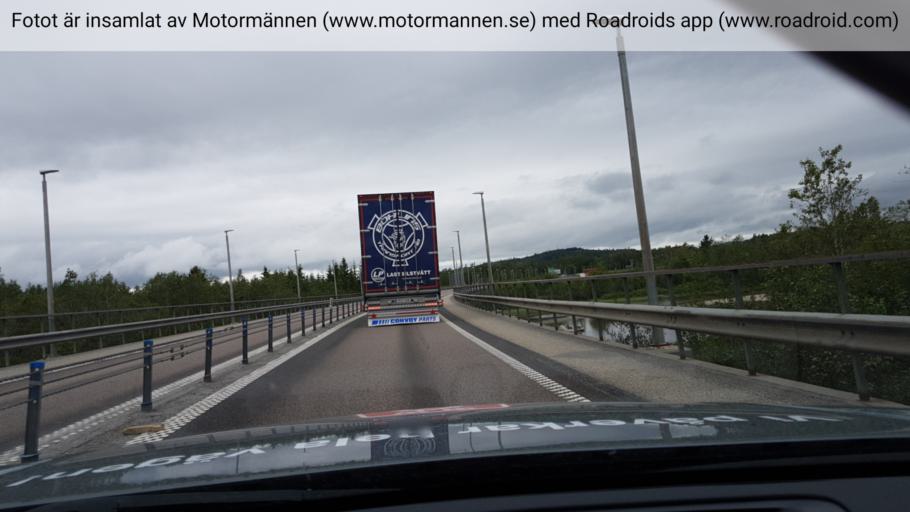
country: SE
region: Vaesternorrland
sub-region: Timra Kommun
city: Soraker
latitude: 62.5171
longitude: 17.4564
